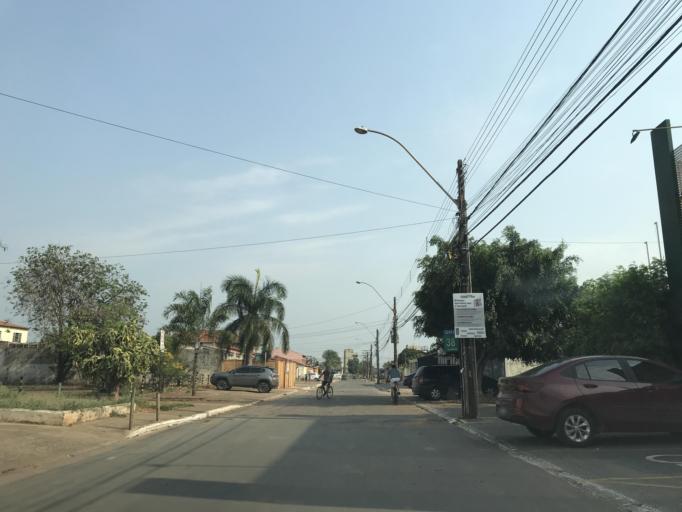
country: BR
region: Federal District
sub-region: Brasilia
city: Brasilia
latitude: -15.8046
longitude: -48.0627
